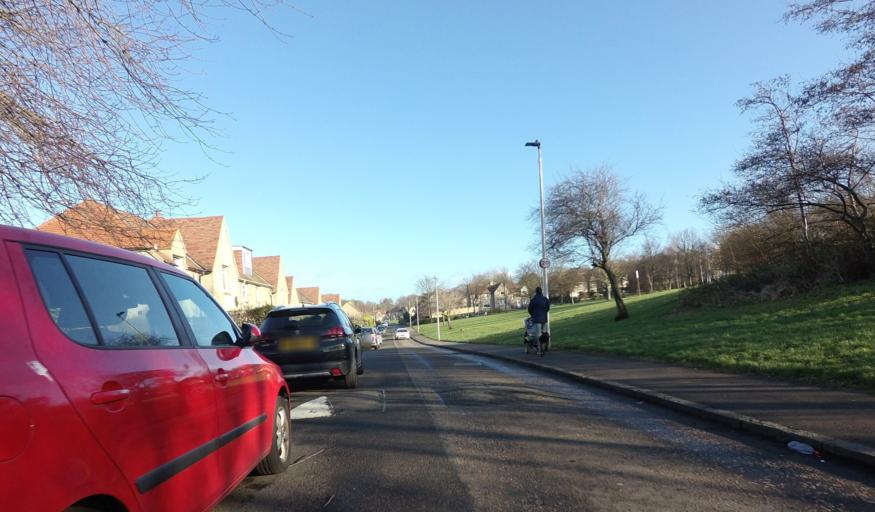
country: GB
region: Scotland
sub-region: Edinburgh
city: Colinton
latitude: 55.9582
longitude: -3.2871
